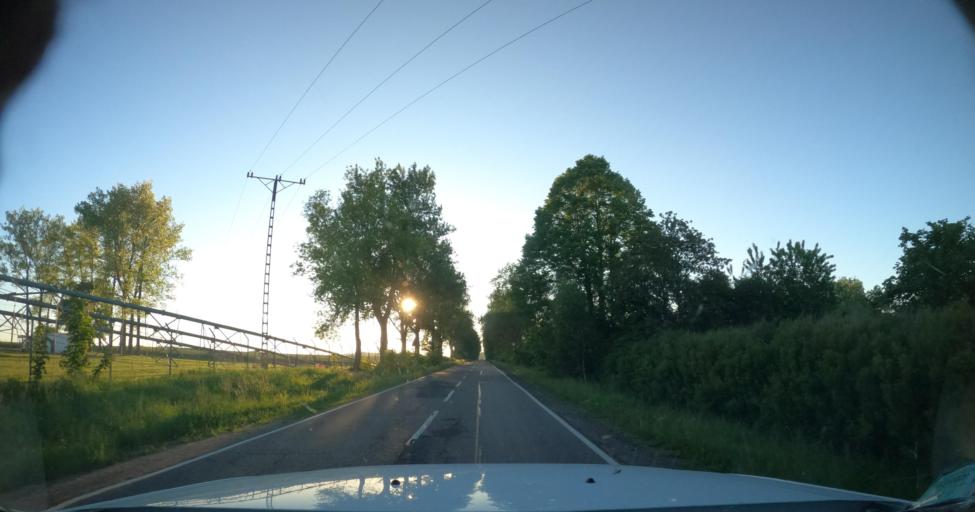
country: PL
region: Pomeranian Voivodeship
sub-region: Powiat slupski
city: Potegowo
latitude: 54.4139
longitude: 17.4137
